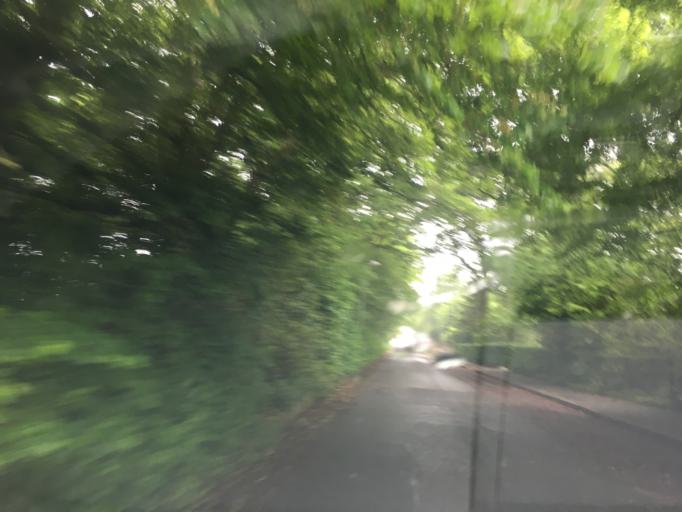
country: GB
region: Scotland
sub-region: Midlothian
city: Loanhead
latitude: 55.8979
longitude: -3.1964
